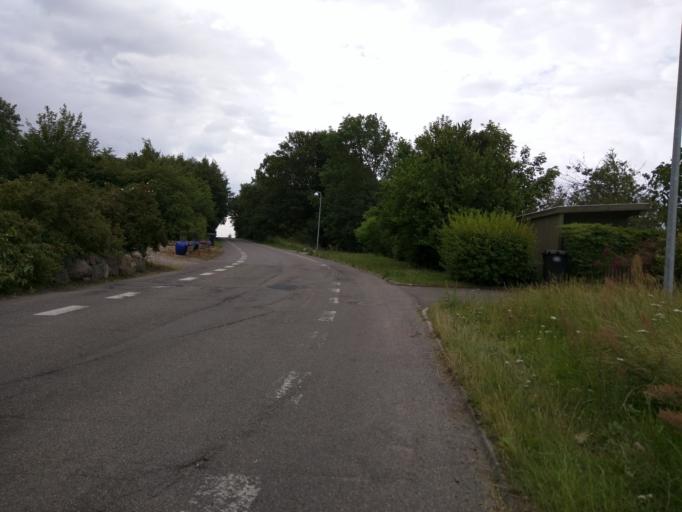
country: DK
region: Zealand
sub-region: Kalundborg Kommune
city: Svebolle
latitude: 55.7127
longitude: 11.3016
